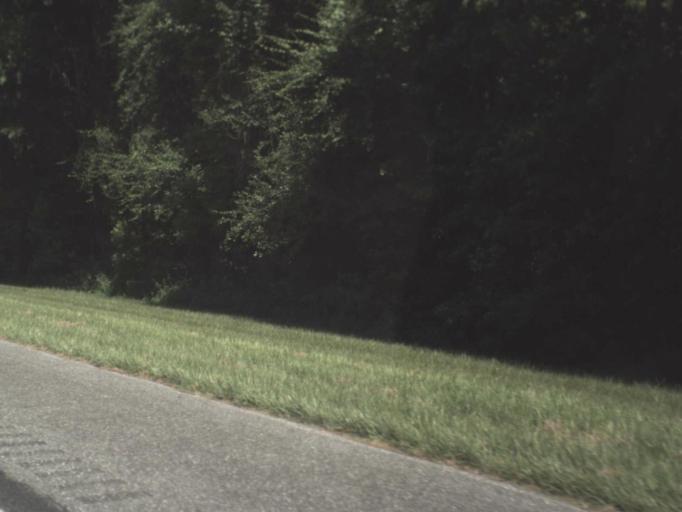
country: US
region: Florida
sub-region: Jefferson County
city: Monticello
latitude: 30.4447
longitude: -83.6803
